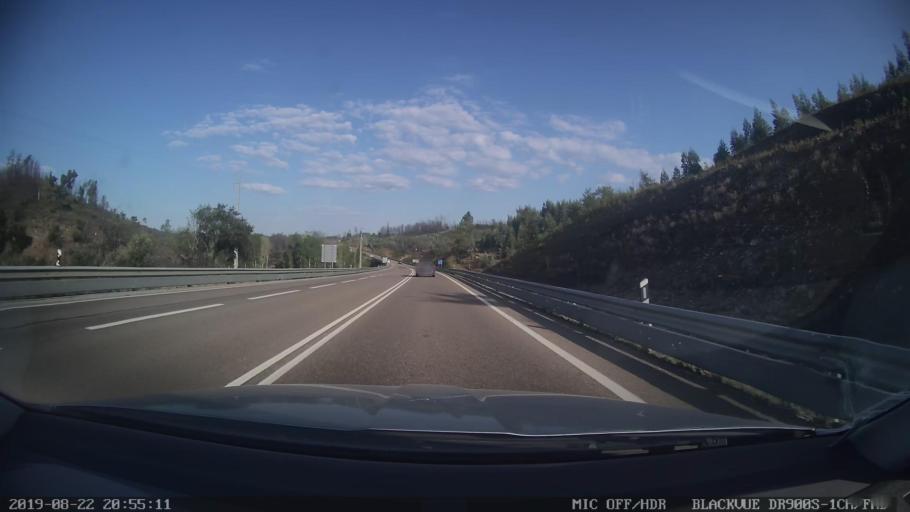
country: PT
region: Castelo Branco
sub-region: Serta
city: Serta
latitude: 39.7788
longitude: -8.0275
